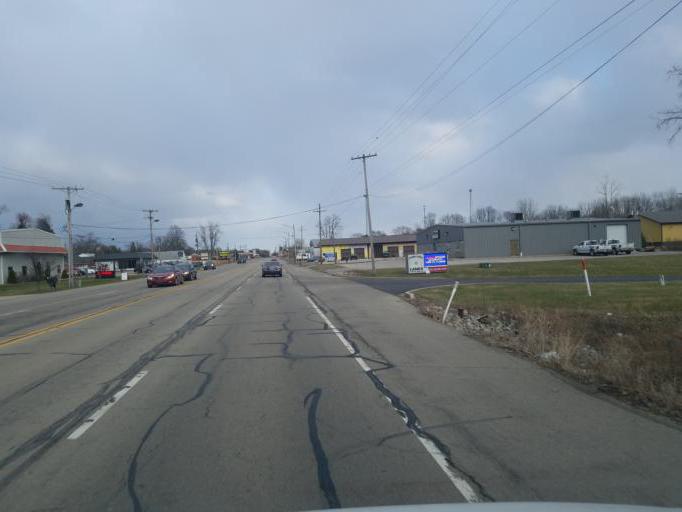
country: US
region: Indiana
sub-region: Hancock County
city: Greenfield
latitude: 39.7840
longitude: -85.7929
